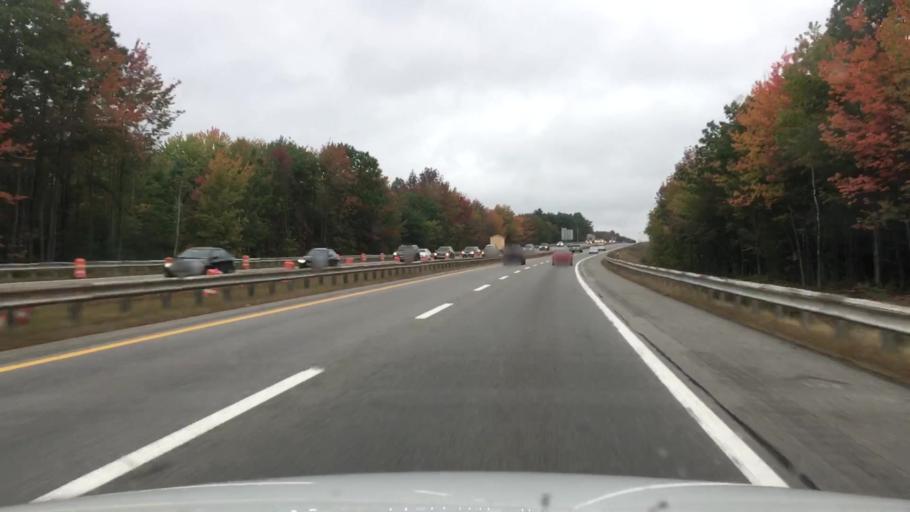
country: US
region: Maine
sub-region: Cumberland County
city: Westbrook
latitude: 43.6955
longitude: -70.3184
